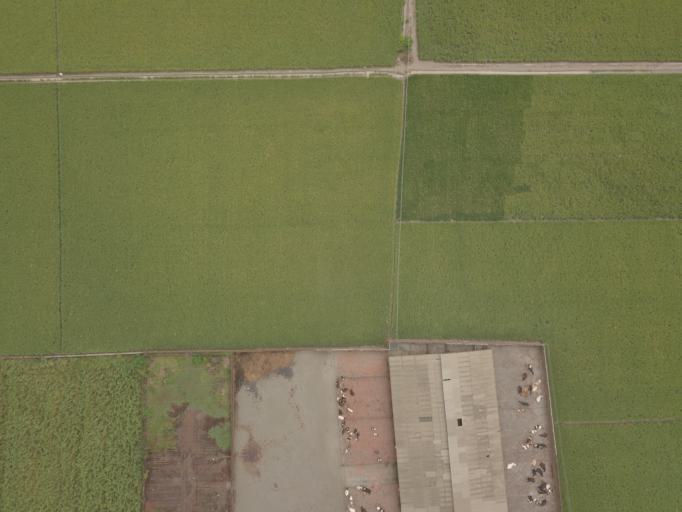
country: IN
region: Punjab
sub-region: Shahid Bhagat Singh Nagar
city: Rahon
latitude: 31.0180
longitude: 76.0943
